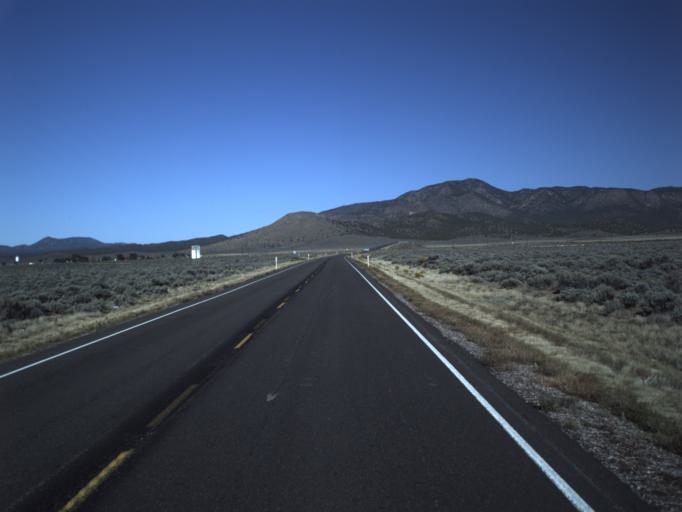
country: US
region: Utah
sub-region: Washington County
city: Enterprise
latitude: 37.7967
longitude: -113.9058
